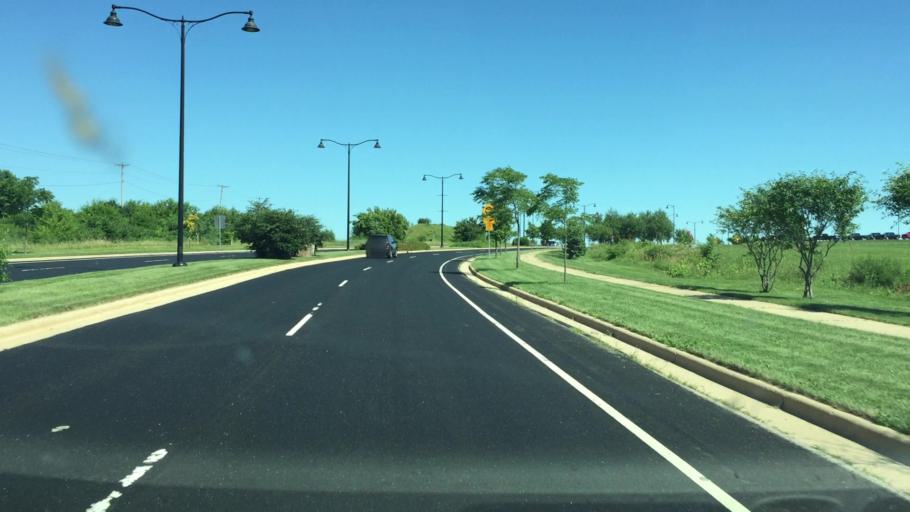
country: US
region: Wisconsin
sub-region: Dane County
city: Mount Horeb
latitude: 43.0078
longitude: -89.7062
